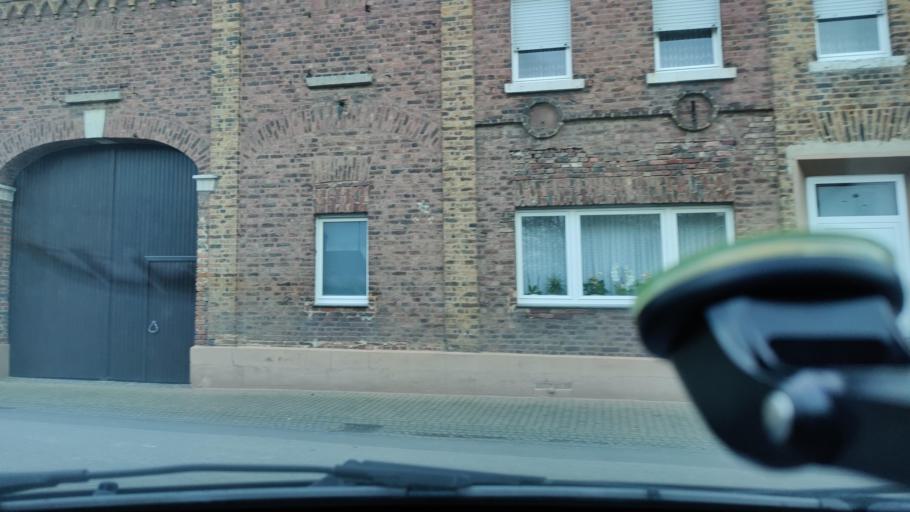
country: DE
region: North Rhine-Westphalia
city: Julich
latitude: 50.9624
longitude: 6.3749
